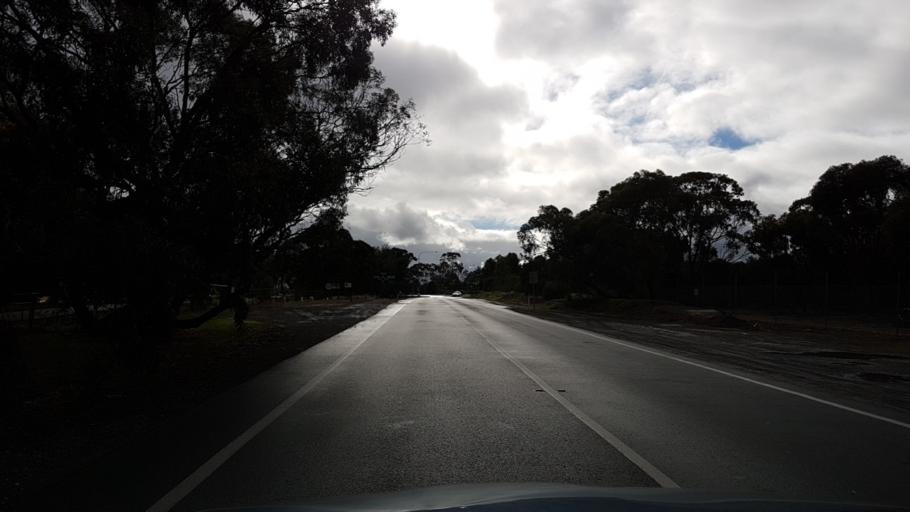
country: AU
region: South Australia
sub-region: Onkaparinga
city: Bedford Park
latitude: -35.0528
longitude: 138.5713
